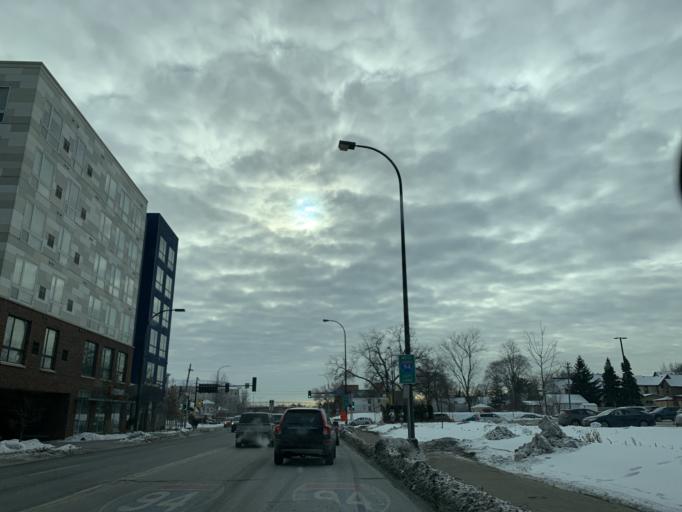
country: US
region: Minnesota
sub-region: Ramsey County
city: Lauderdale
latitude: 44.9711
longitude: -93.2229
